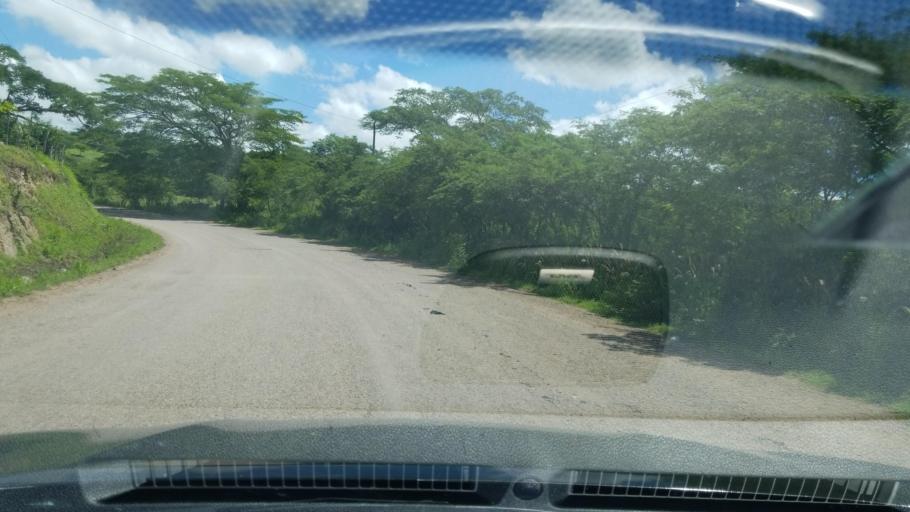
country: HN
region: Francisco Morazan
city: San Juan de Flores
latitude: 14.3107
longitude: -87.0363
